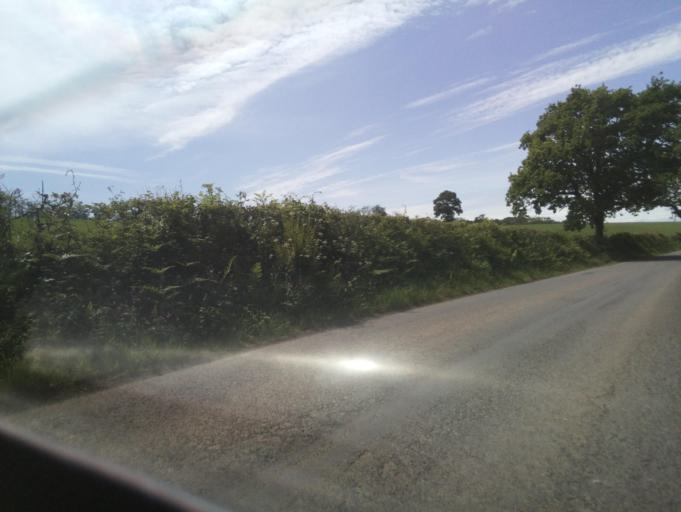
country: GB
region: England
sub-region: Devon
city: Kingsbridge
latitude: 50.3618
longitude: -3.7672
